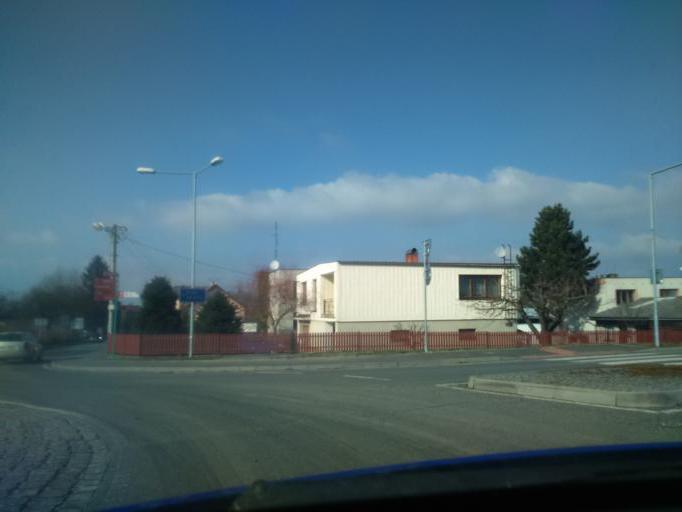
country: CZ
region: Plzensky
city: Horsovsky Tyn
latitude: 49.5221
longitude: 12.9471
